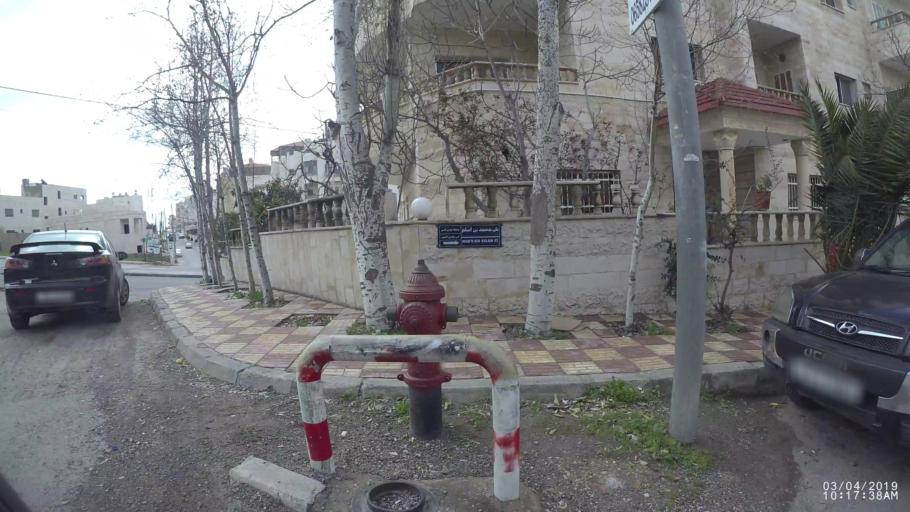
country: JO
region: Amman
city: Wadi as Sir
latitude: 31.9469
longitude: 35.8277
